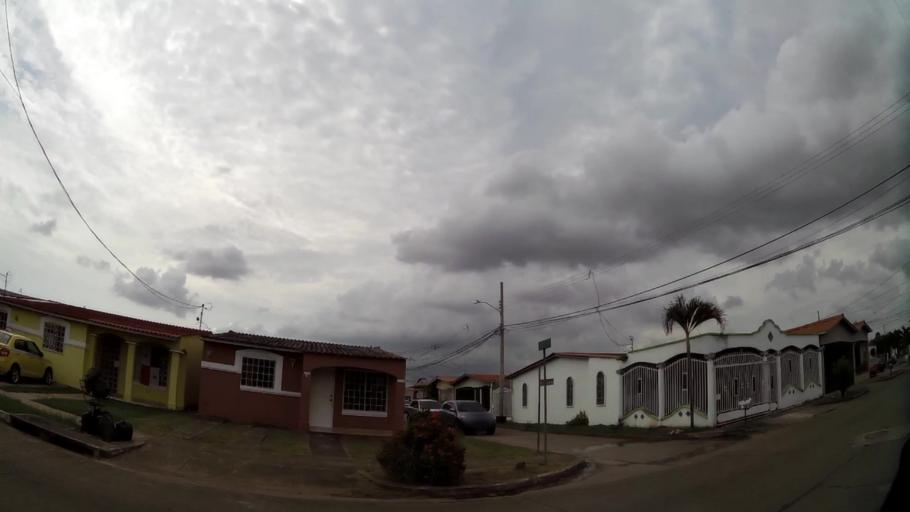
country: PA
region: Panama
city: Tocumen
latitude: 9.0442
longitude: -79.4103
